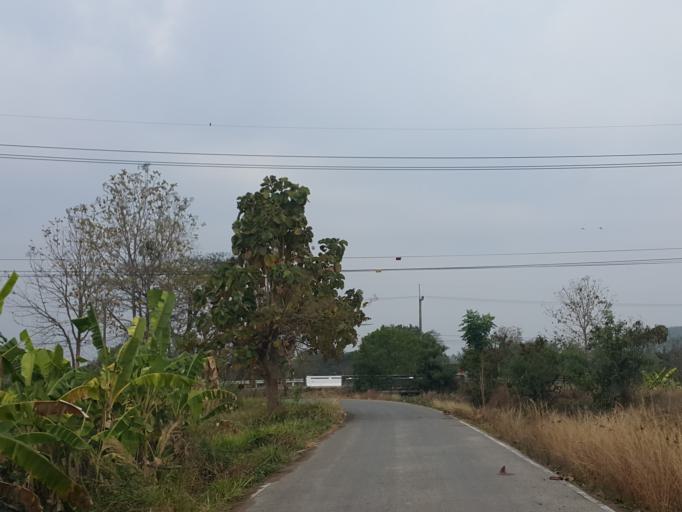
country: TH
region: Chiang Mai
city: San Kamphaeng
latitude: 18.7299
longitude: 99.1909
